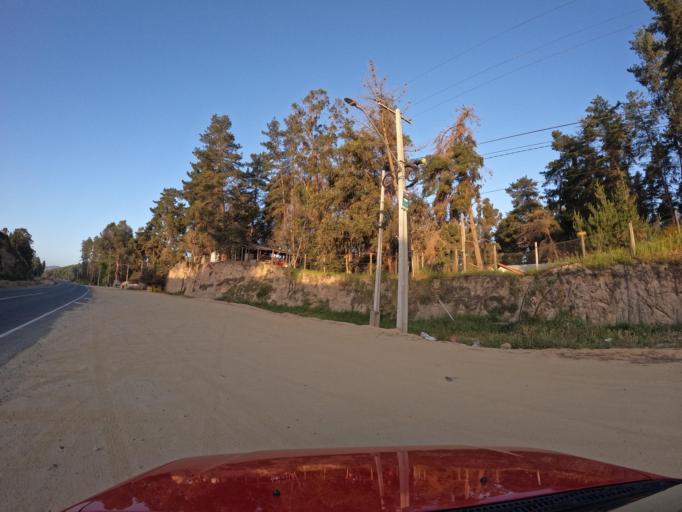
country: CL
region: O'Higgins
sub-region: Provincia de Cachapoal
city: San Vicente
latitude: -34.1449
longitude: -71.3796
